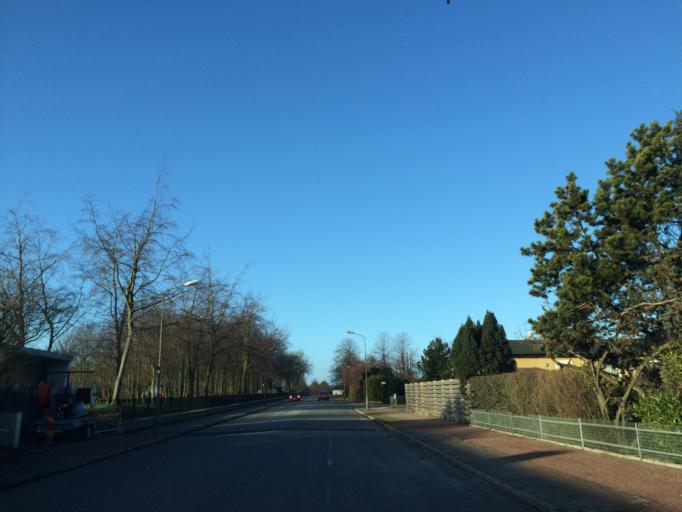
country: SE
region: Skane
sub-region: Malmo
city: Bunkeflostrand
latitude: 55.5747
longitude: 12.9502
